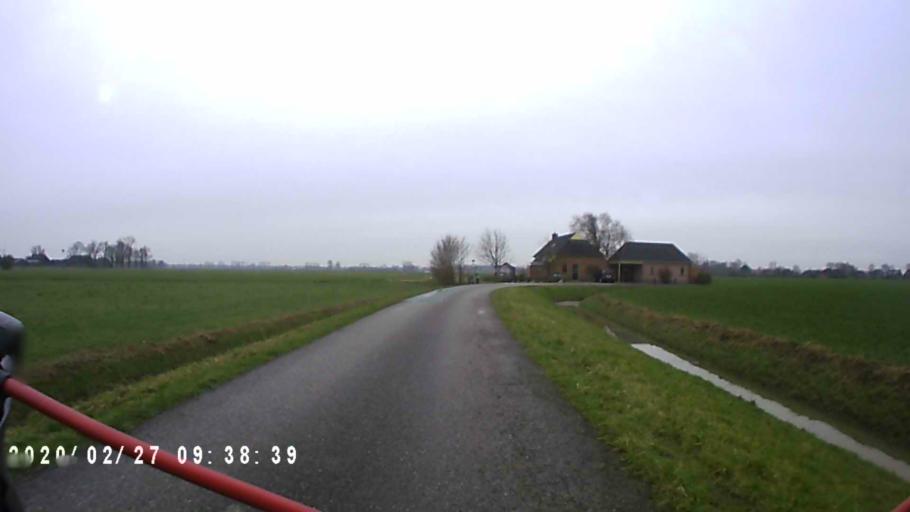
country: NL
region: Groningen
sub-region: Gemeente Zuidhorn
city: Aduard
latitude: 53.2790
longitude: 6.4302
